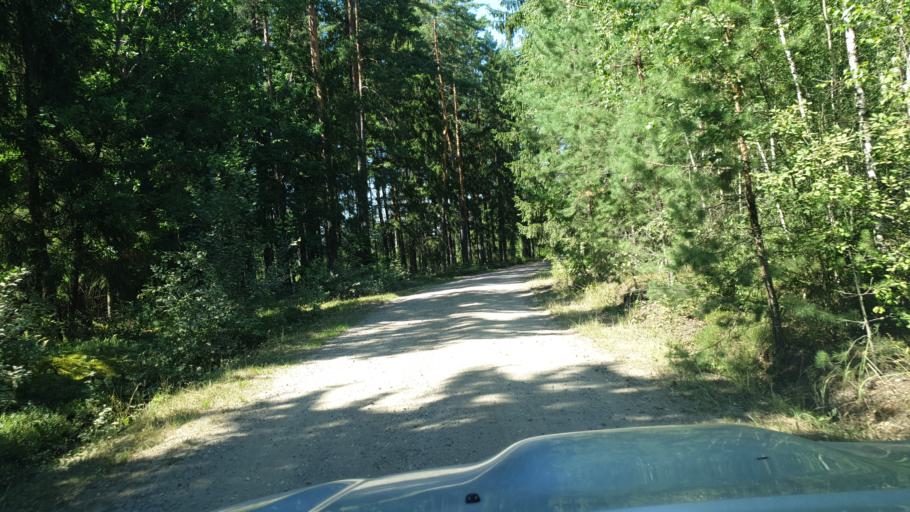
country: LT
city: Sirvintos
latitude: 54.9116
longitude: 24.9293
